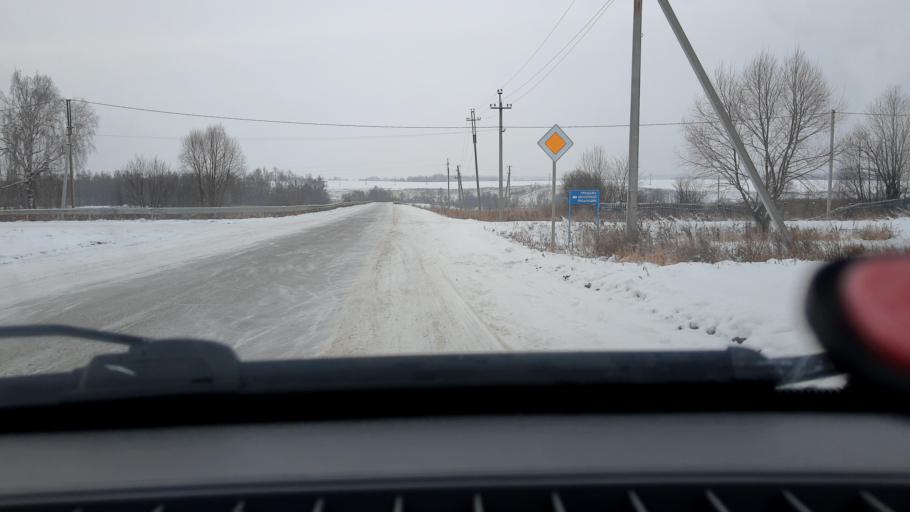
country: RU
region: Bashkortostan
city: Iglino
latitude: 54.6442
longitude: 56.4249
